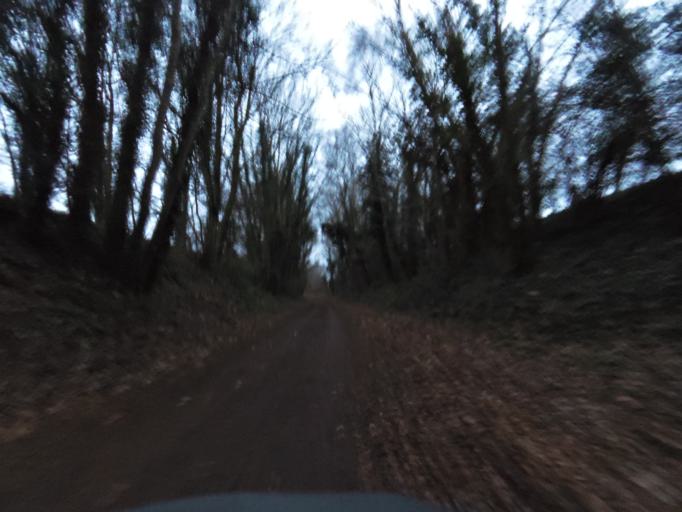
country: GB
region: England
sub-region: Norfolk
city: Costessey
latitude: 52.6800
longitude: 1.2164
